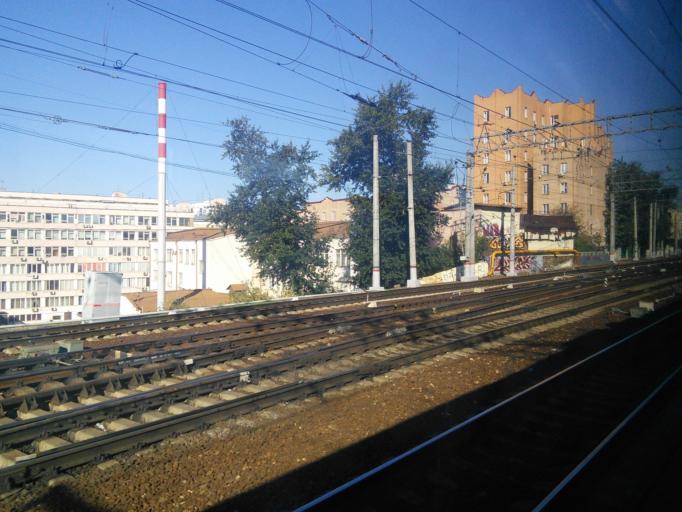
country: RU
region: Moscow
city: Taganskiy
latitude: 55.7526
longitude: 37.6669
